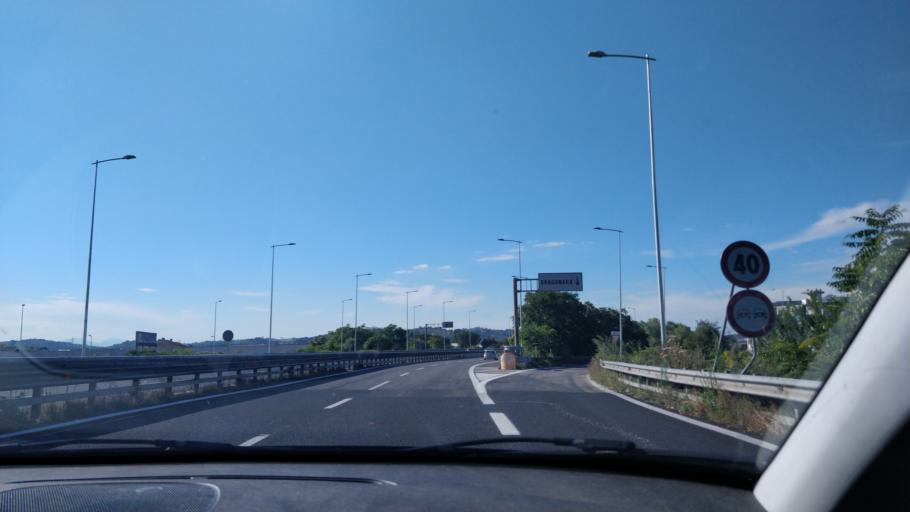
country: IT
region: Abruzzo
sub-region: Provincia di Pescara
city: Santa Teresa
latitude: 42.4051
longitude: 14.1626
